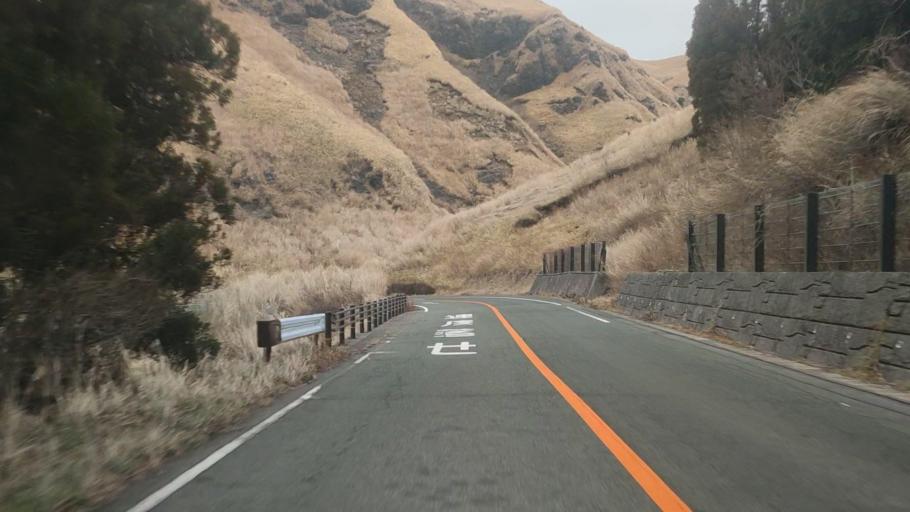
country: JP
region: Kumamoto
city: Aso
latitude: 32.9100
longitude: 131.1431
